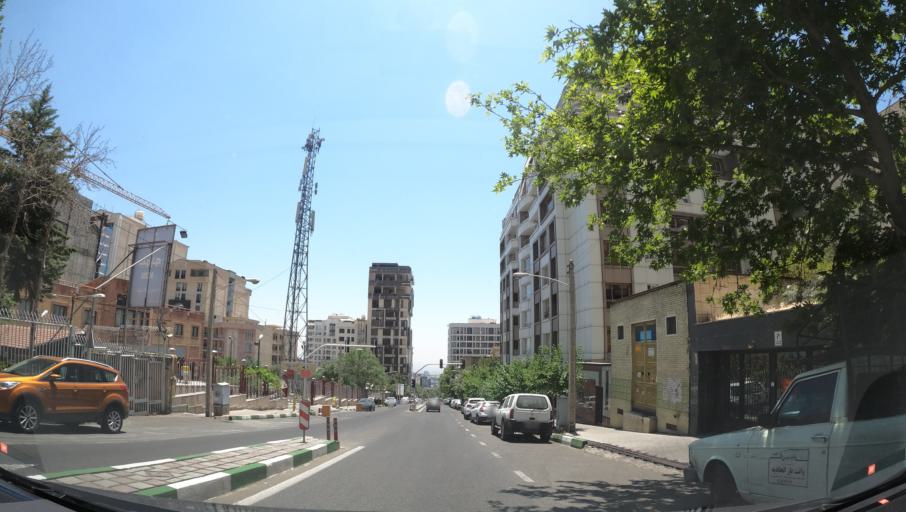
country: IR
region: Tehran
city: Tajrish
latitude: 35.8081
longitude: 51.4010
